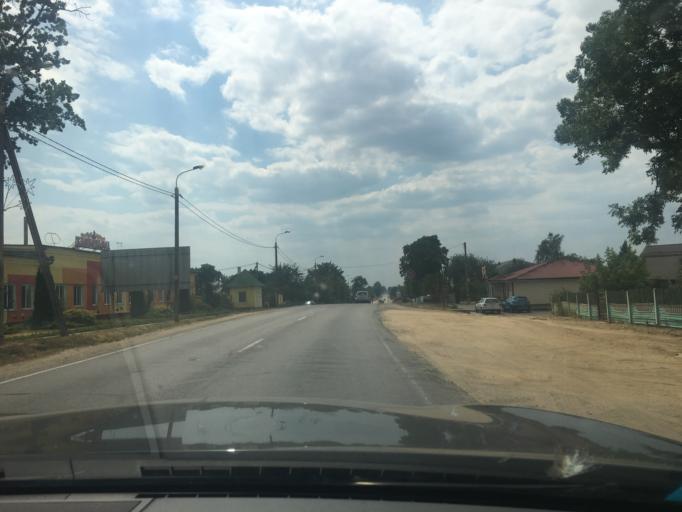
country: BY
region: Brest
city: Pruzhany
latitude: 52.5532
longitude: 24.4740
